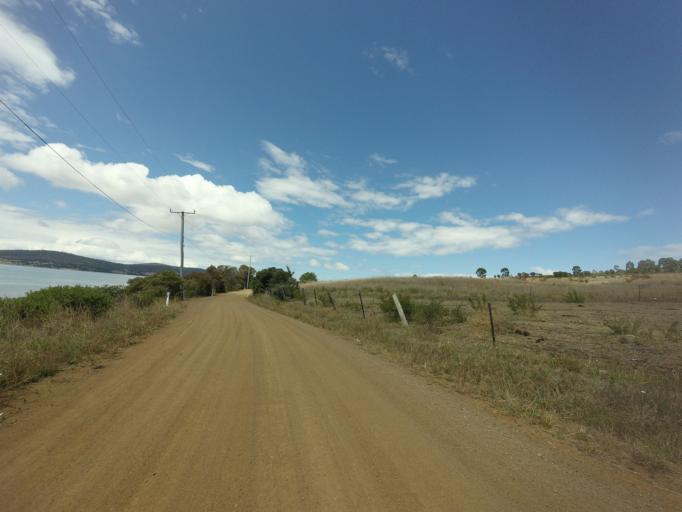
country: AU
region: Tasmania
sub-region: Clarence
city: Rokeby
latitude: -42.9120
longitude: 147.4317
